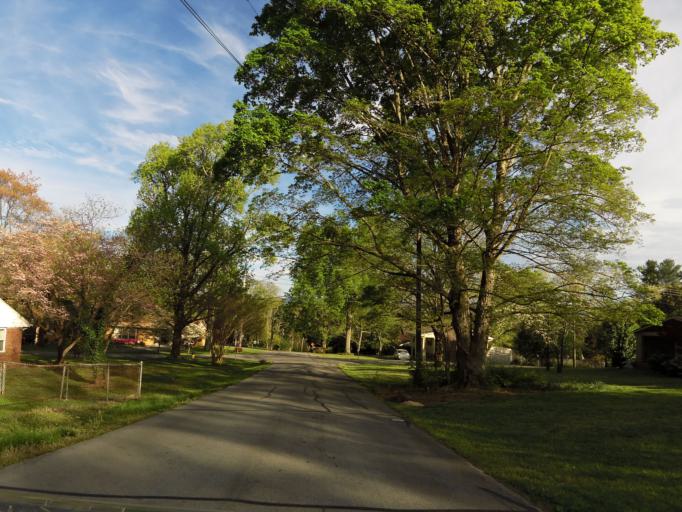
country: US
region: Tennessee
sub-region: Blount County
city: Maryville
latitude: 35.7364
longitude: -83.9848
